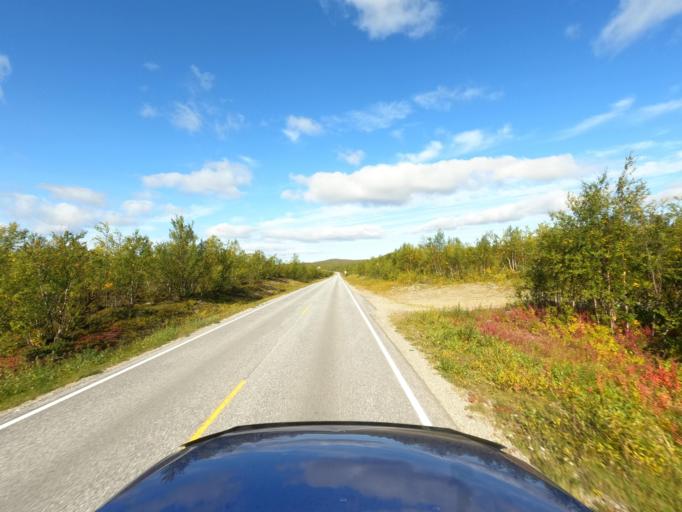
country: NO
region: Finnmark Fylke
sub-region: Karasjok
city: Karasjohka
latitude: 69.5350
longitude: 25.4342
